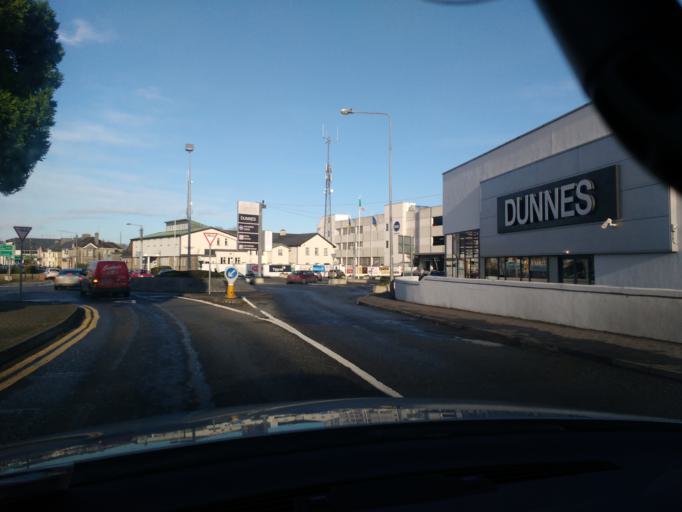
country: IE
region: Munster
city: Thurles
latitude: 52.6748
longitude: -7.8121
